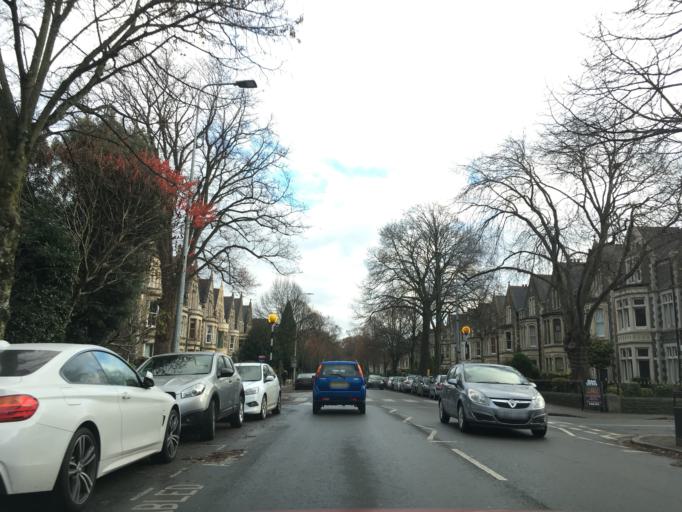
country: GB
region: Wales
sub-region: Cardiff
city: Cardiff
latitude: 51.4876
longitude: -3.1980
